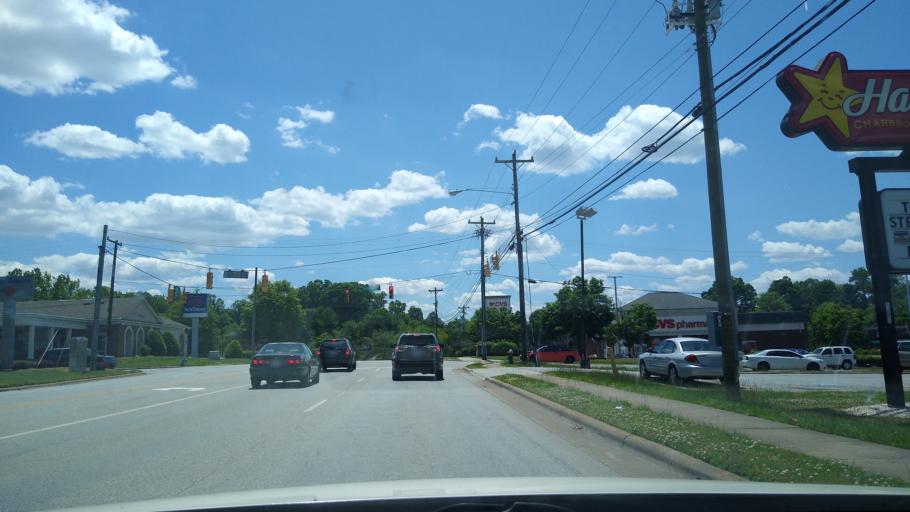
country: US
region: North Carolina
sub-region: Guilford County
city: Greensboro
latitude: 36.0883
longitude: -79.8884
